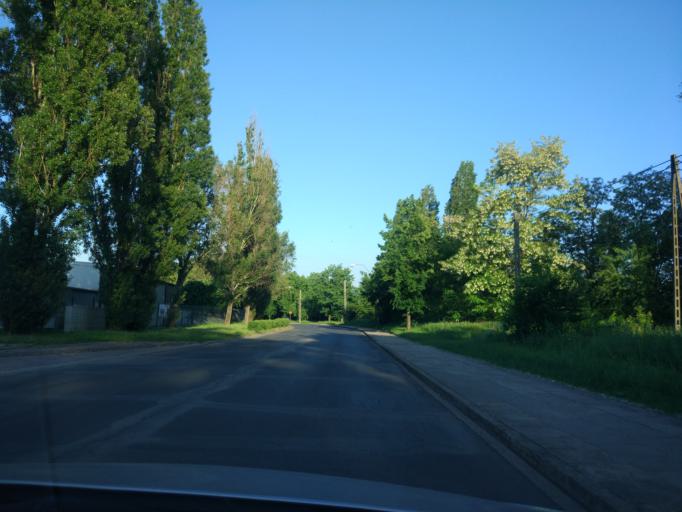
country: PL
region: Lodz Voivodeship
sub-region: Powiat kutnowski
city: Kutno
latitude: 52.2256
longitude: 19.3555
